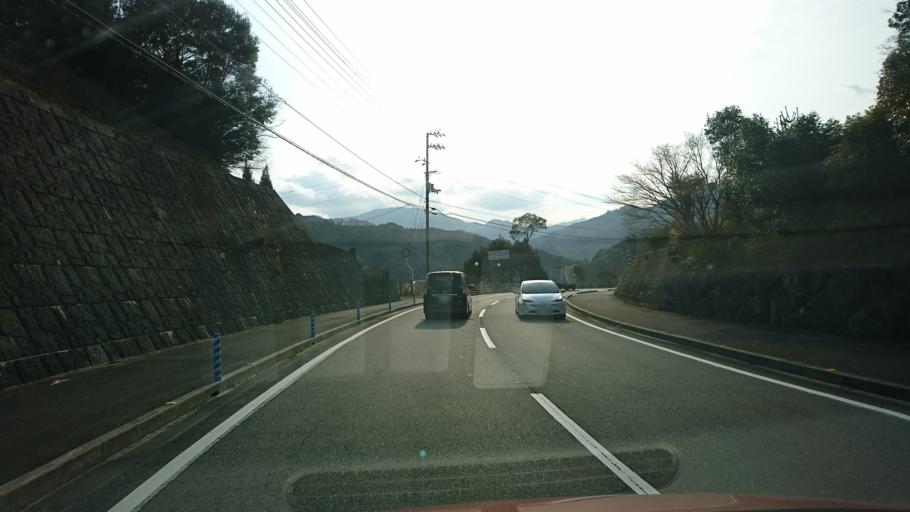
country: JP
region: Ehime
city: Hojo
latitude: 33.9949
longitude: 132.9207
